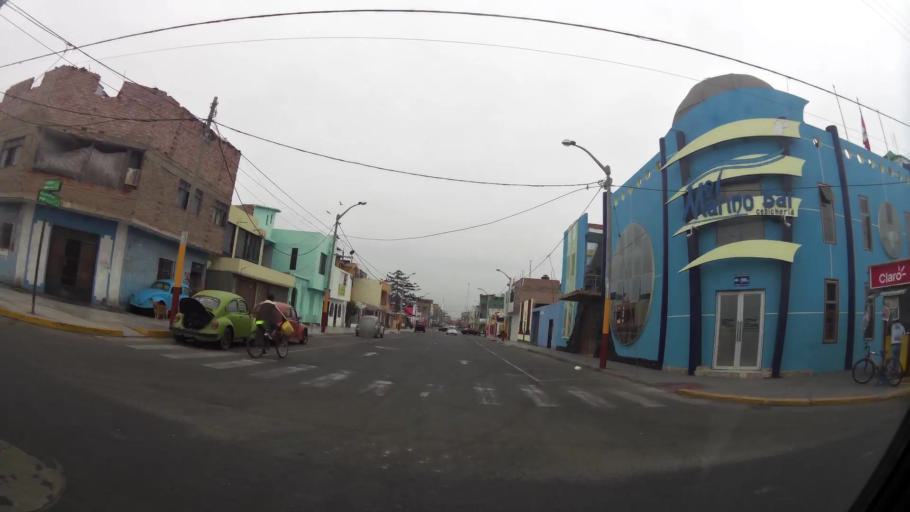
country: PE
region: Ancash
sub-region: Provincia de Santa
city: Chimbote
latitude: -9.0730
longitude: -78.5971
